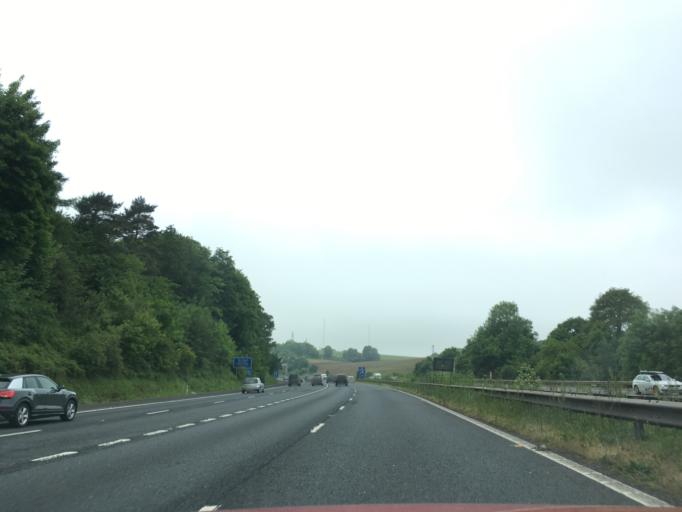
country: GB
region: England
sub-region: Devon
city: Exminster
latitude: 50.6855
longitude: -3.5049
